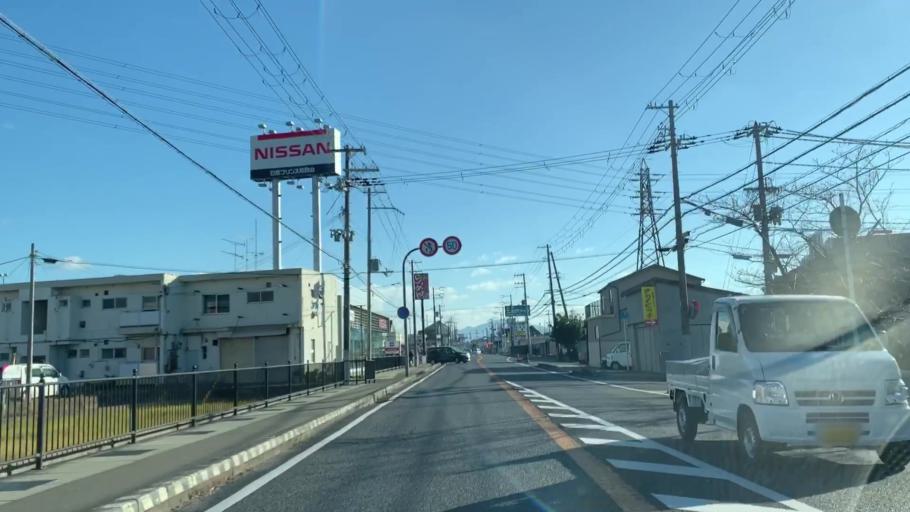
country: JP
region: Wakayama
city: Wakayama-shi
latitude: 34.2449
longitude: 135.2035
